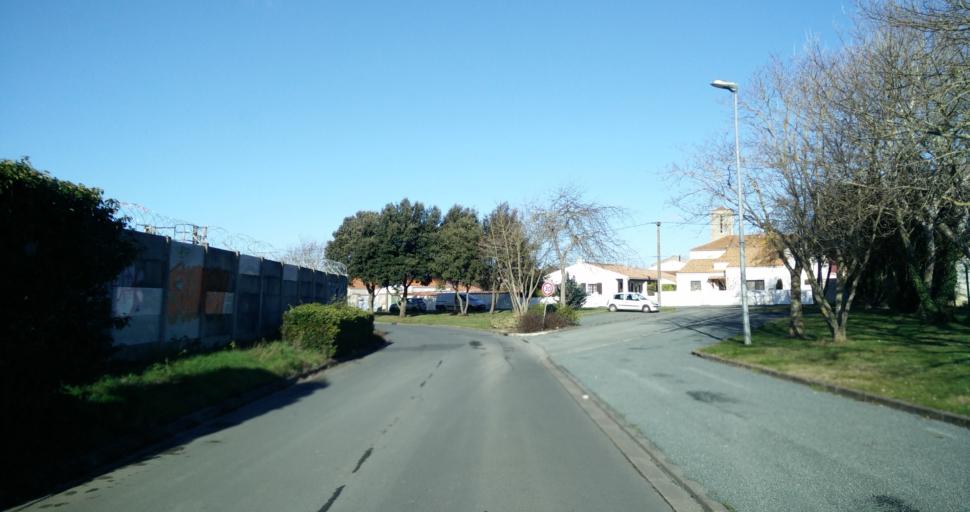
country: FR
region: Poitou-Charentes
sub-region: Departement de la Charente-Maritime
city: Lagord
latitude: 46.1690
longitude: -1.2038
